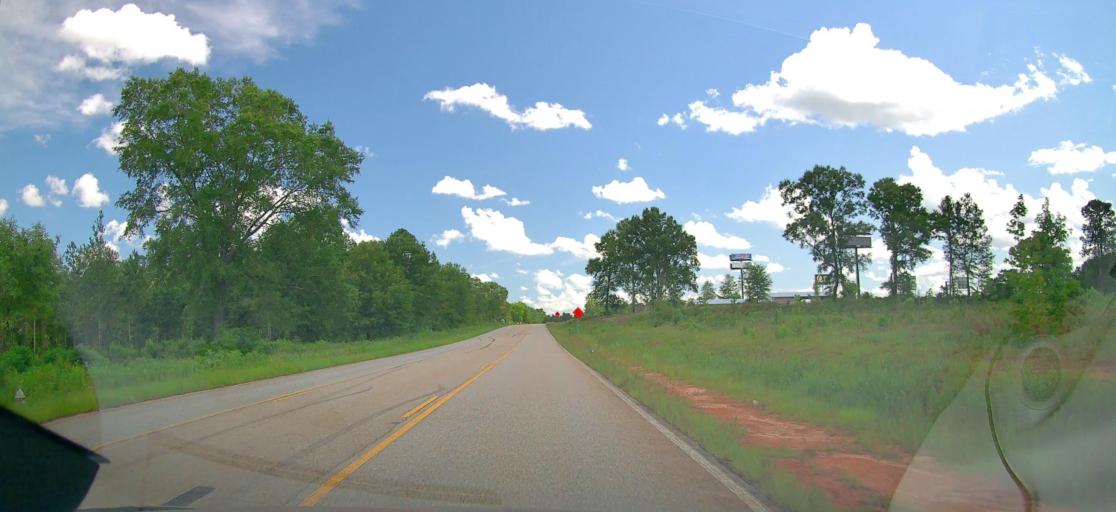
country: US
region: Georgia
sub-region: Peach County
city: Byron
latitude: 32.6053
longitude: -83.7406
